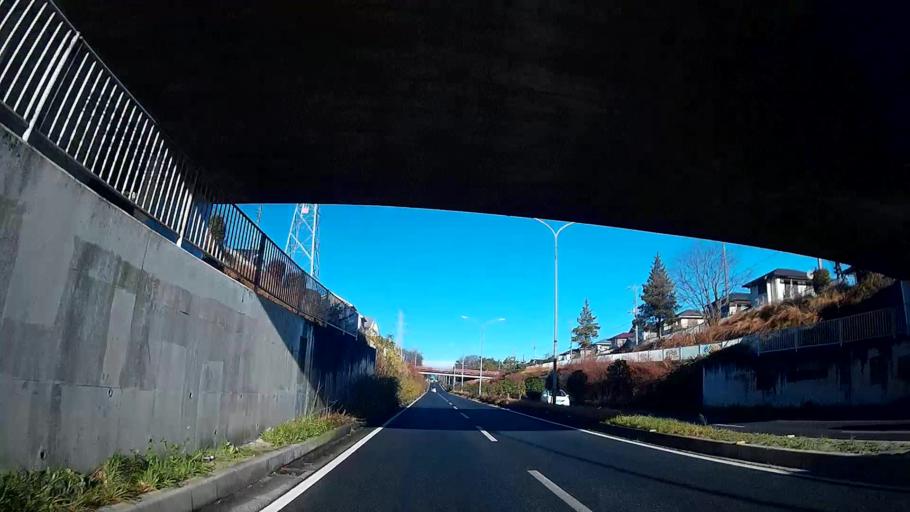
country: JP
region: Saitama
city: Hanno
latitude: 35.8523
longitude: 139.3609
